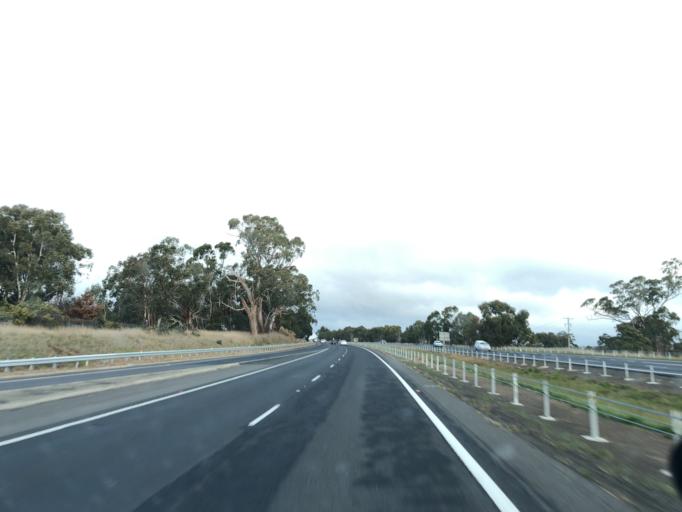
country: AU
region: Victoria
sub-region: Mount Alexander
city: Castlemaine
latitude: -37.2608
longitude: 144.4720
